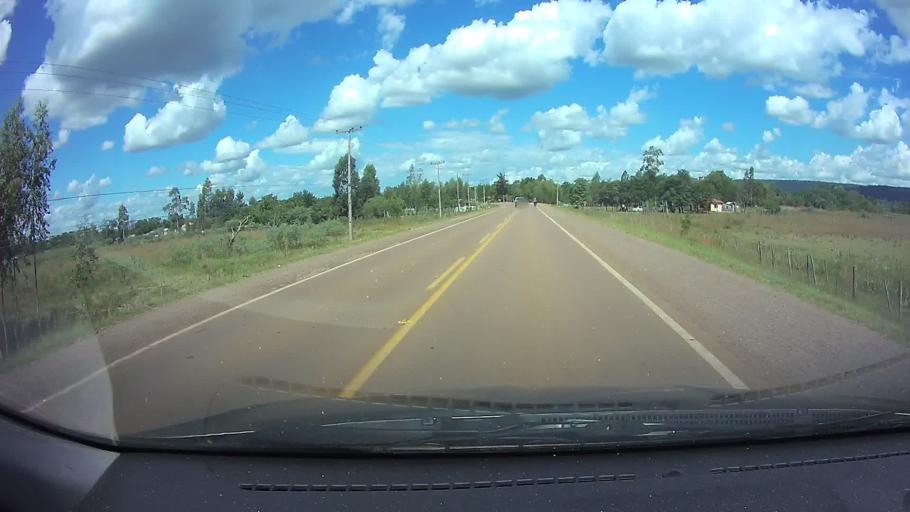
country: PY
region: Guaira
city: Itape
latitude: -25.9154
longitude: -56.6944
